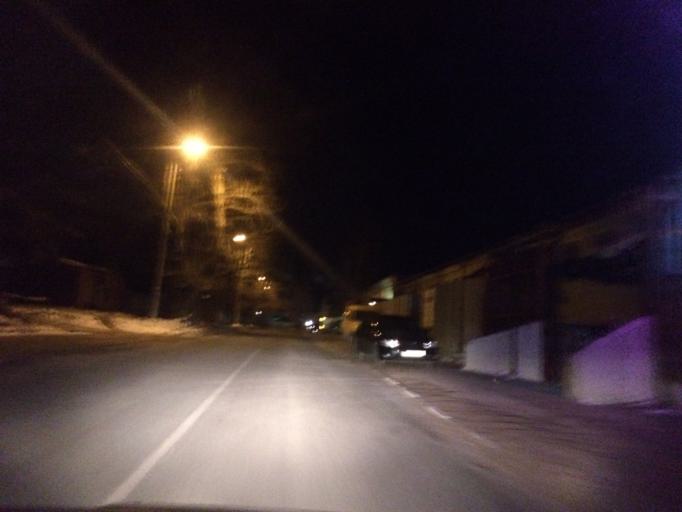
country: RU
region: Tula
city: Mendeleyevskiy
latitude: 54.1622
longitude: 37.5715
